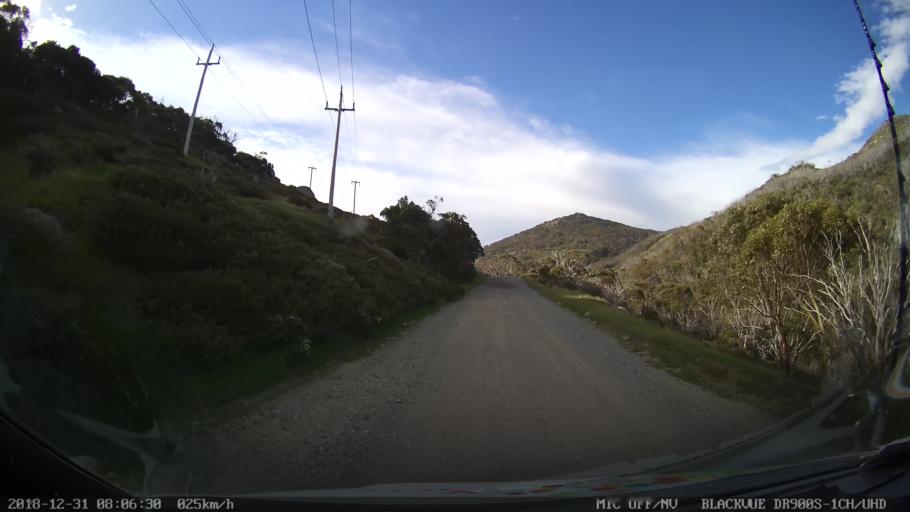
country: AU
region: New South Wales
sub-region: Snowy River
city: Jindabyne
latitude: -36.3749
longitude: 148.4082
